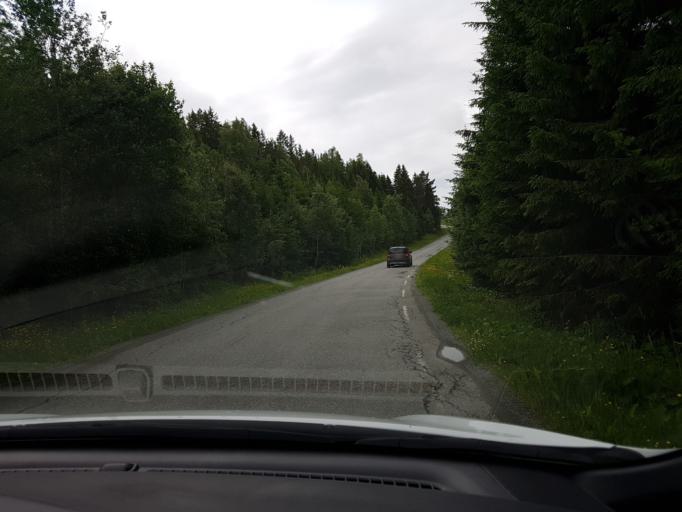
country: NO
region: Nord-Trondelag
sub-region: Frosta
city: Frosta
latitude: 63.6190
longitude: 10.7586
